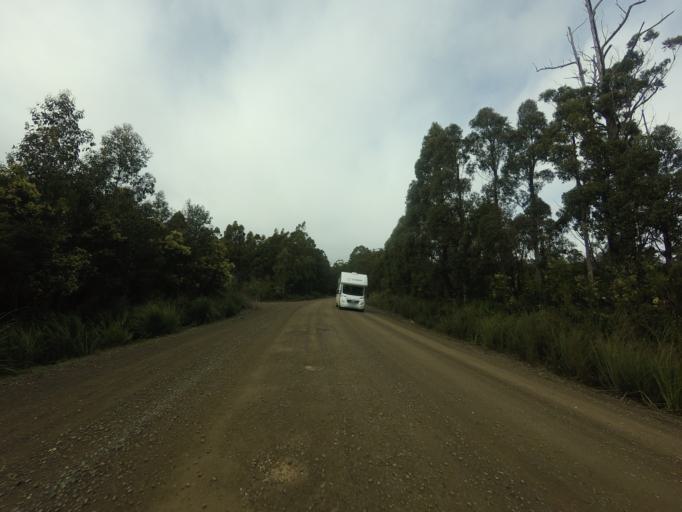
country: AU
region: Tasmania
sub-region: Huon Valley
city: Geeveston
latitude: -43.5112
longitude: 146.8856
